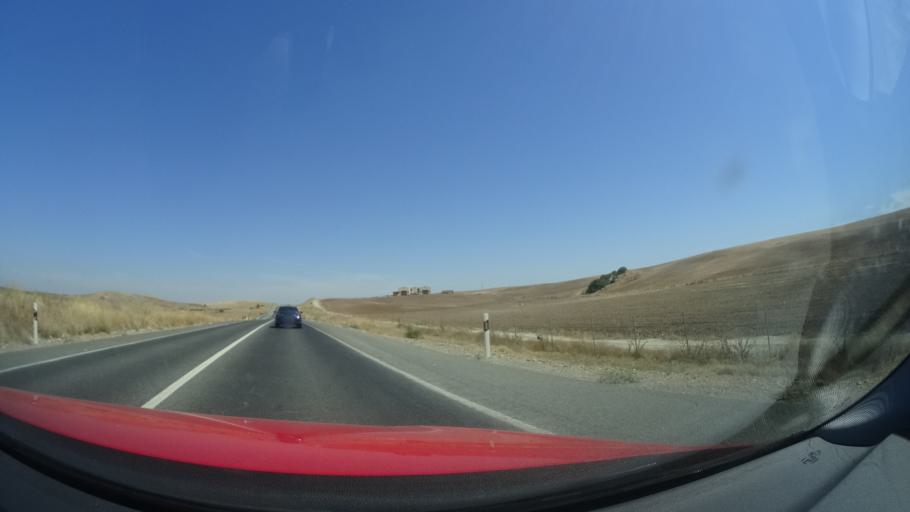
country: ES
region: Andalusia
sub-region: Provincia de Sevilla
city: Las Cabezas de San Juan
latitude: 36.9595
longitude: -5.8894
